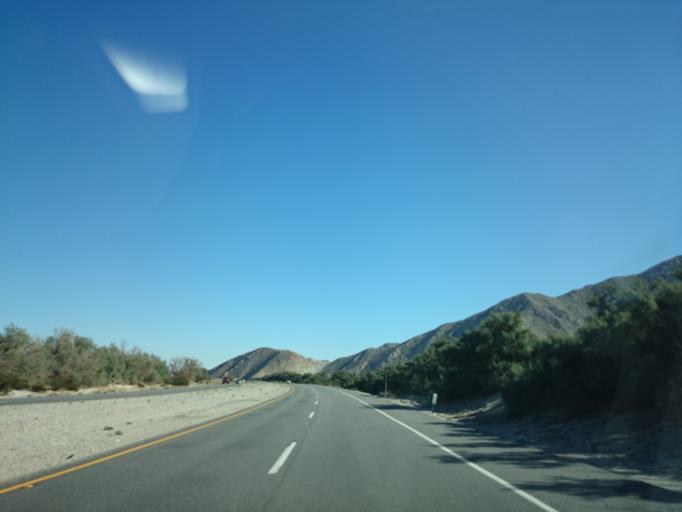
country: US
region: California
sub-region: Riverside County
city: Garnet
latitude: 33.9057
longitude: -116.6505
